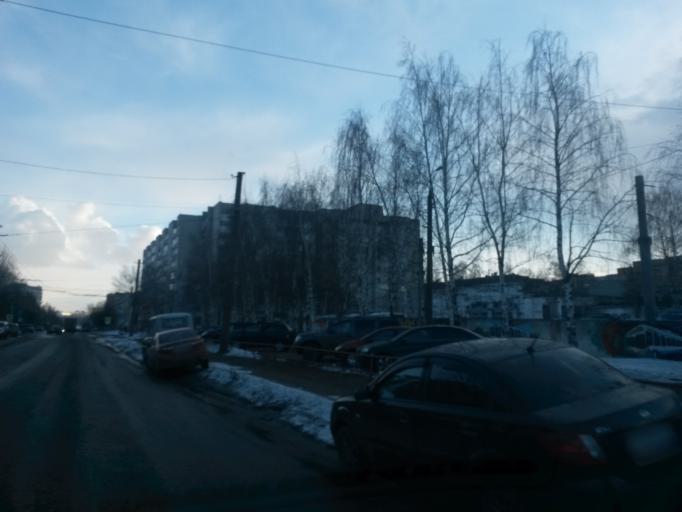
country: RU
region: Jaroslavl
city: Yaroslavl
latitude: 57.6260
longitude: 39.8485
